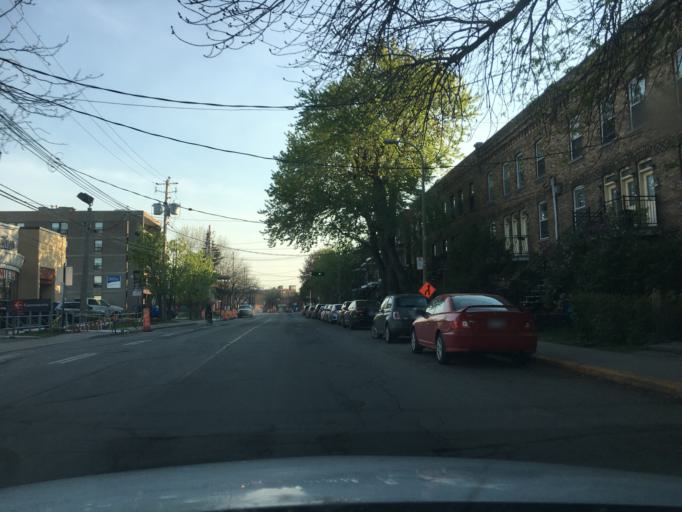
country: CA
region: Quebec
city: Westmount
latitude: 45.4698
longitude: -73.5649
